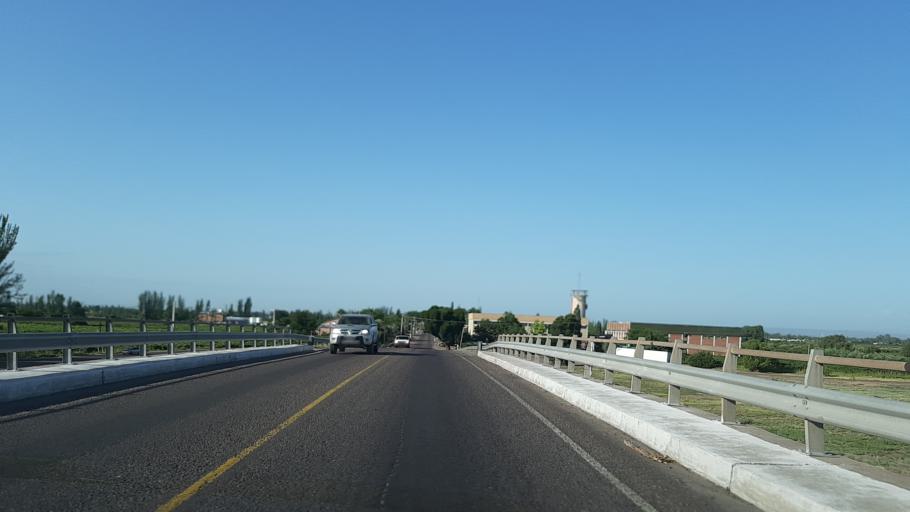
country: AR
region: Mendoza
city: San Martin
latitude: -33.0408
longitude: -68.5203
